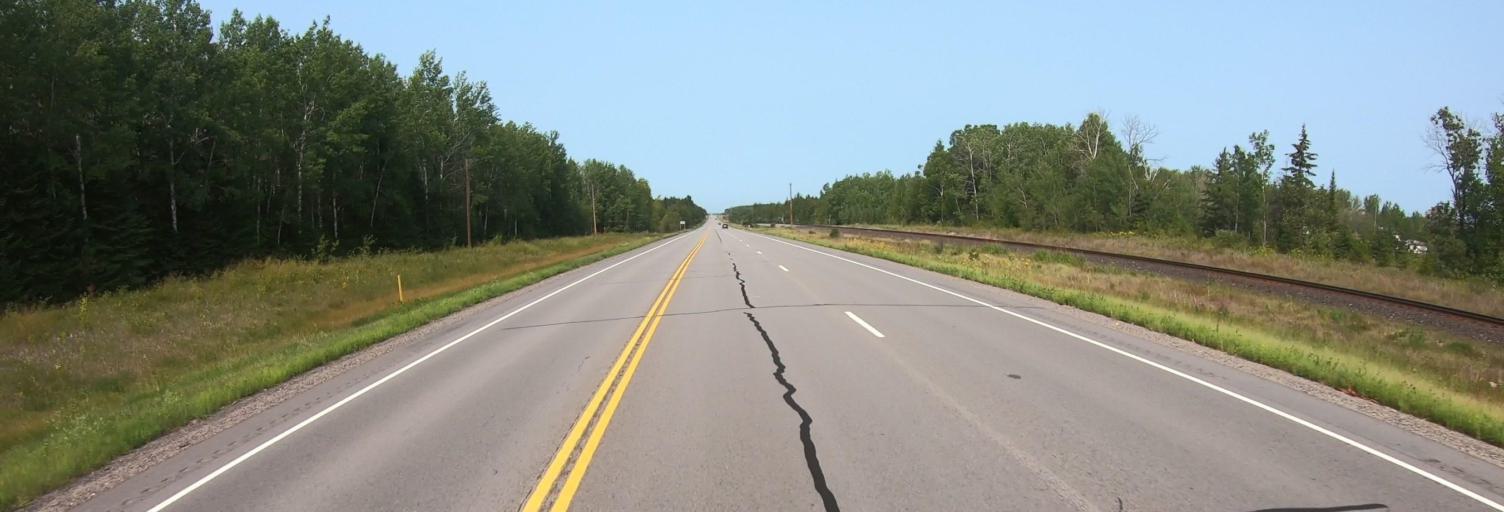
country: CA
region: Ontario
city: Fort Frances
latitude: 48.4505
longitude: -93.2713
